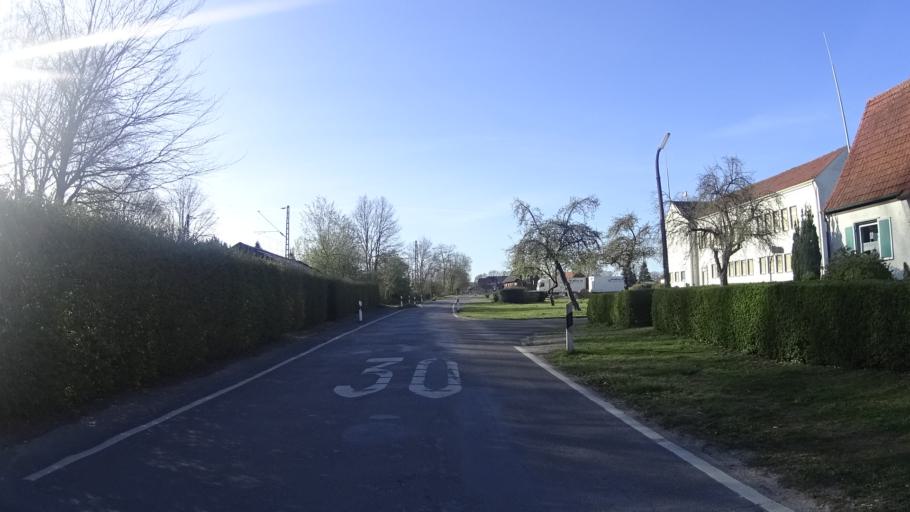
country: DE
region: North Rhine-Westphalia
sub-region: Regierungsbezirk Munster
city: Greven
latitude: 52.0855
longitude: 7.6010
